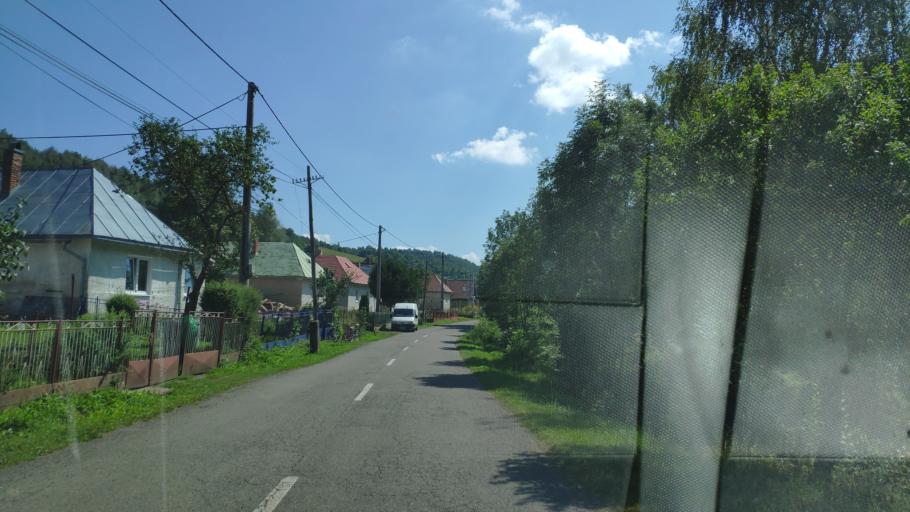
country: PL
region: Subcarpathian Voivodeship
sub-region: Powiat leski
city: Cisna
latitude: 49.0507
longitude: 22.3547
